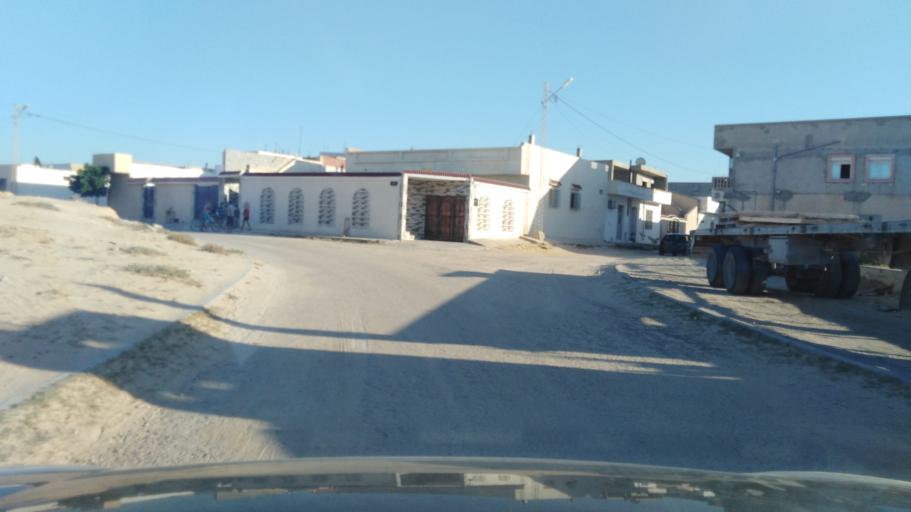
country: TN
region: Qabis
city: Gabes
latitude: 33.9544
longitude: 10.0096
